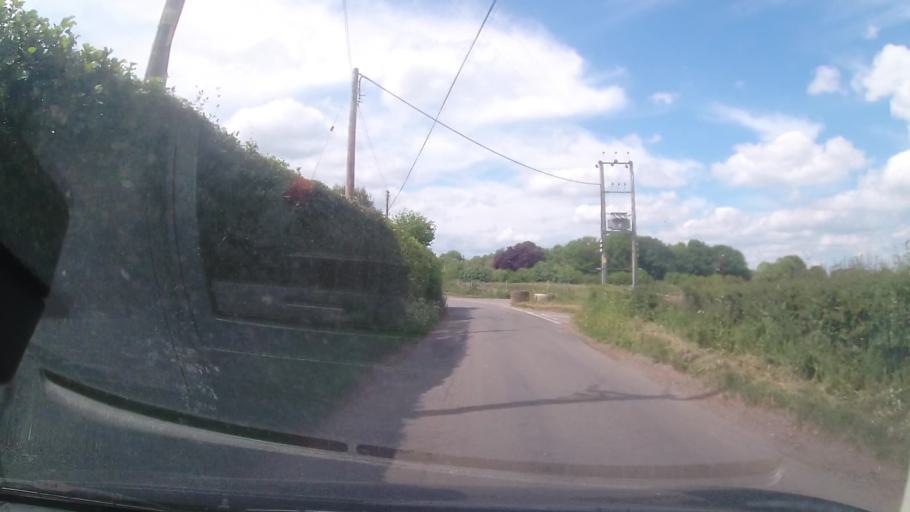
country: GB
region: England
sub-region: Shropshire
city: Stoke upon Tern
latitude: 52.7931
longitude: -2.5513
